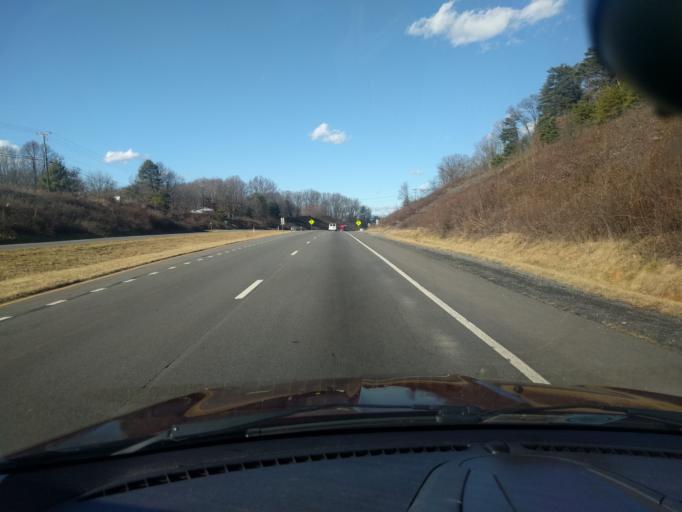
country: US
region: Virginia
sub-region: Botetourt County
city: Cloverdale
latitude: 37.3610
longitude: -79.8858
